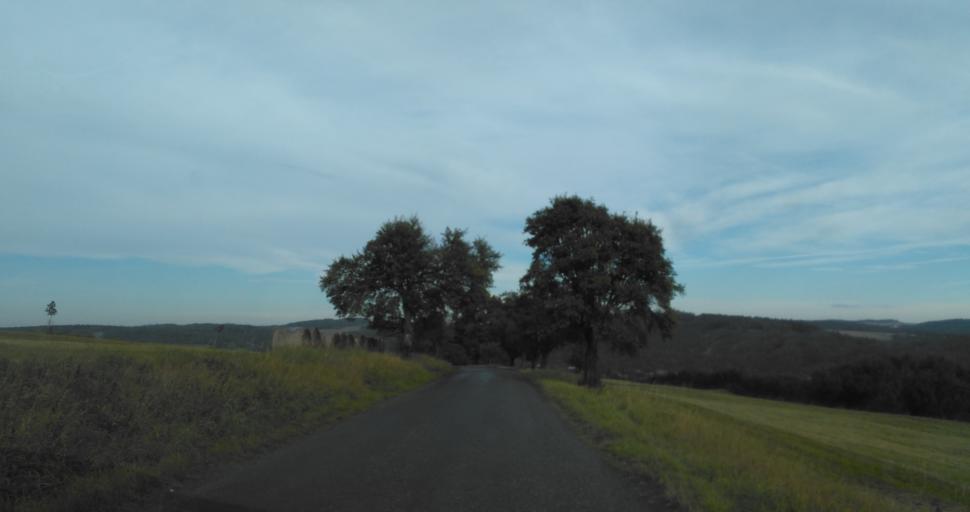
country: CZ
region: Plzensky
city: Zbiroh
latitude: 49.9576
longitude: 13.7736
